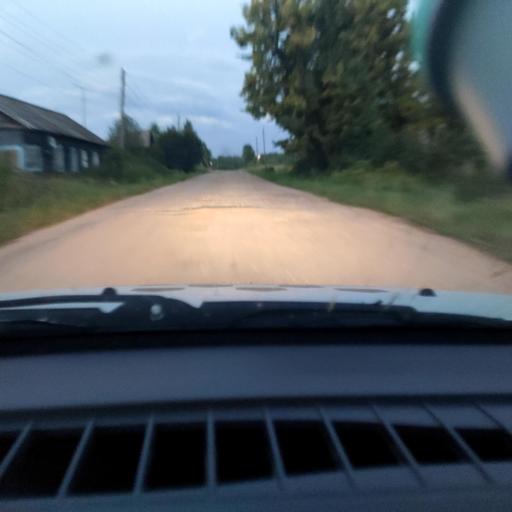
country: RU
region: Kirov
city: Darovskoy
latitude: 58.9891
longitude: 47.8732
